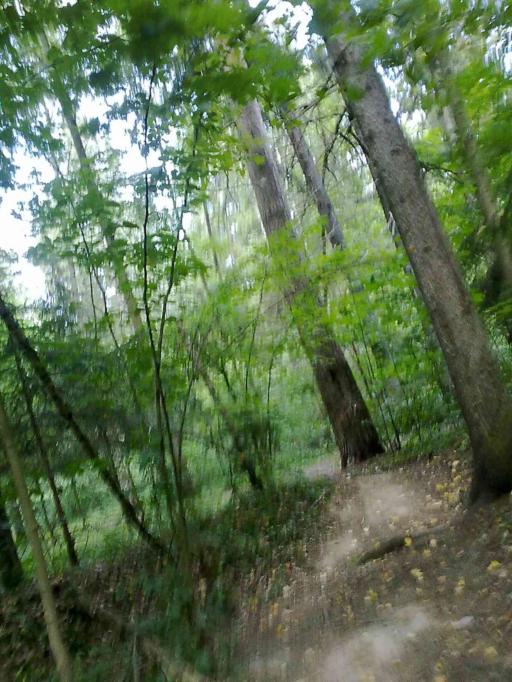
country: RU
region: Moskovskaya
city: Moskovskiy
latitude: 55.5844
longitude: 37.3331
